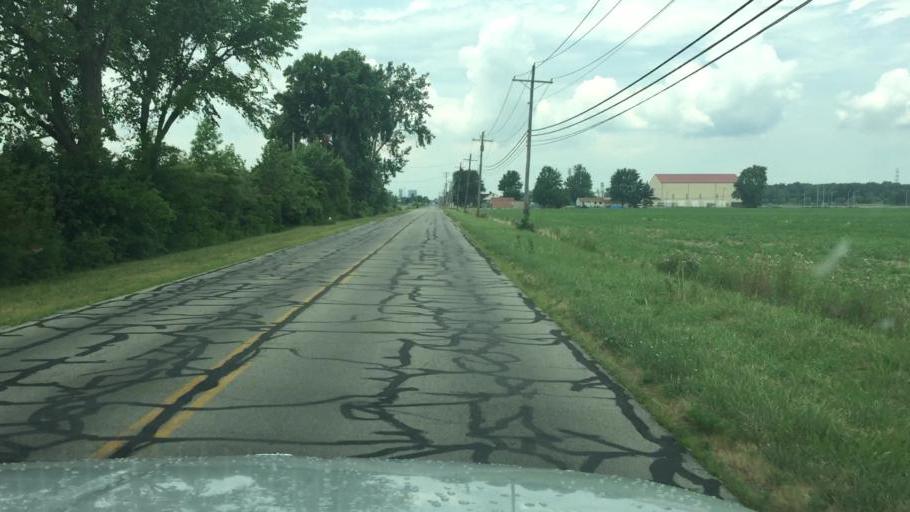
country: US
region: Ohio
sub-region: Wood County
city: Walbridge
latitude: 41.5838
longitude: -83.5278
